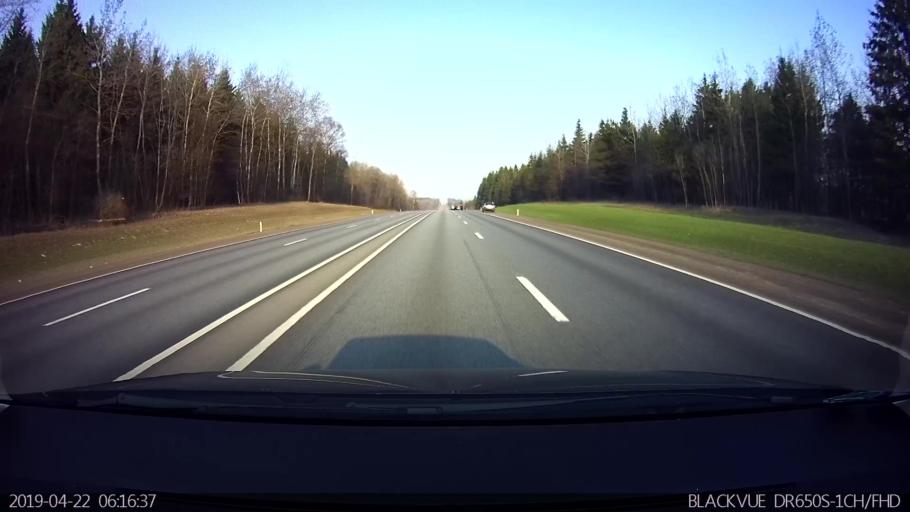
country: RU
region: Moskovskaya
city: Mozhaysk
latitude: 55.4603
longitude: 36.0145
